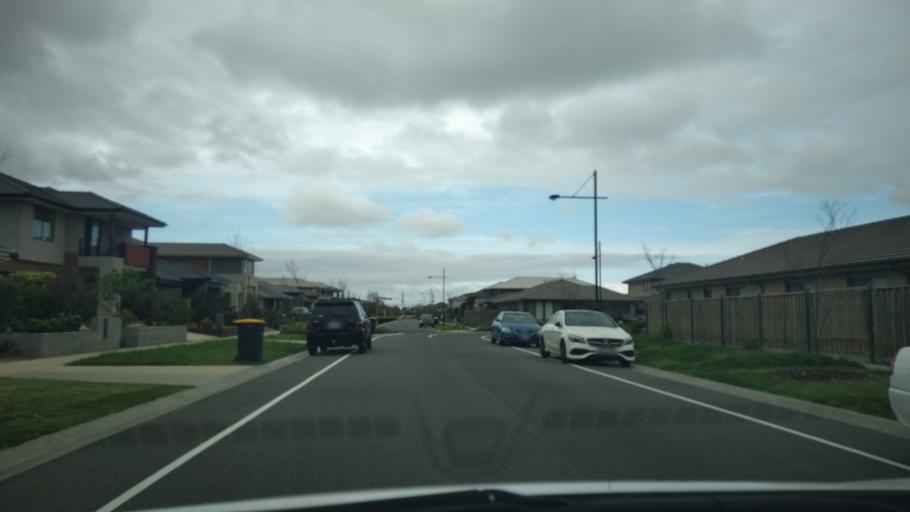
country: AU
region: Victoria
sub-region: Greater Dandenong
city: Keysborough
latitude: -38.0052
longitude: 145.1792
